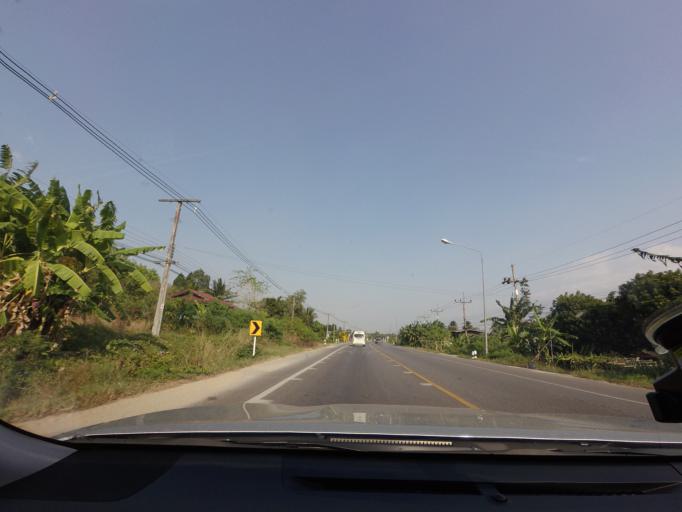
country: TH
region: Surat Thani
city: Phrasaeng
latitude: 8.5738
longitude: 99.2131
